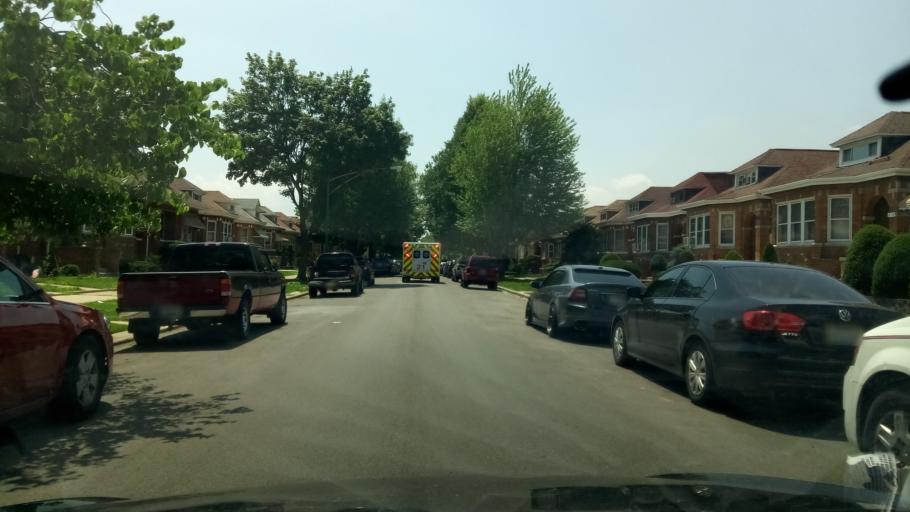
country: US
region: Illinois
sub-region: Cook County
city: Hometown
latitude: 41.7821
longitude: -87.7254
